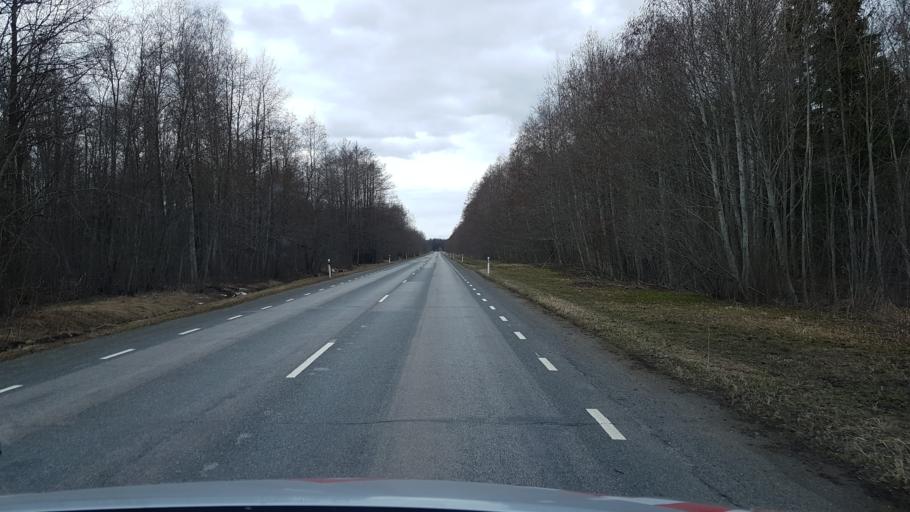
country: EE
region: Ida-Virumaa
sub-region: Narva-Joesuu linn
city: Narva-Joesuu
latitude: 59.3518
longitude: 28.0606
